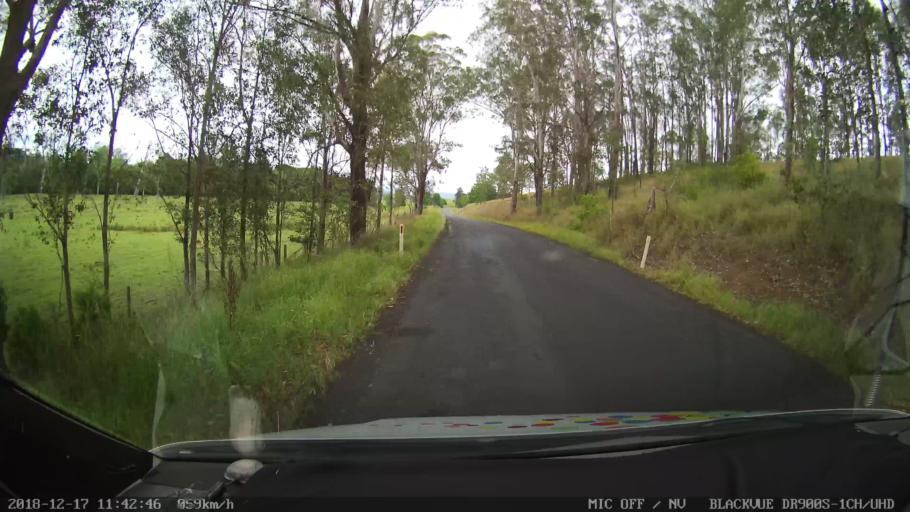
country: AU
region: New South Wales
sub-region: Kyogle
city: Kyogle
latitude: -28.6660
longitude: 152.5924
